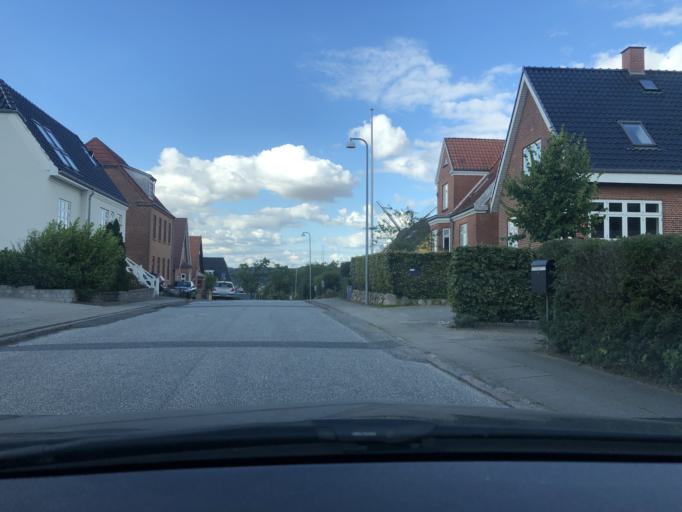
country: DK
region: South Denmark
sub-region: Vejle Kommune
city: Vejle
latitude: 55.6986
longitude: 9.5298
